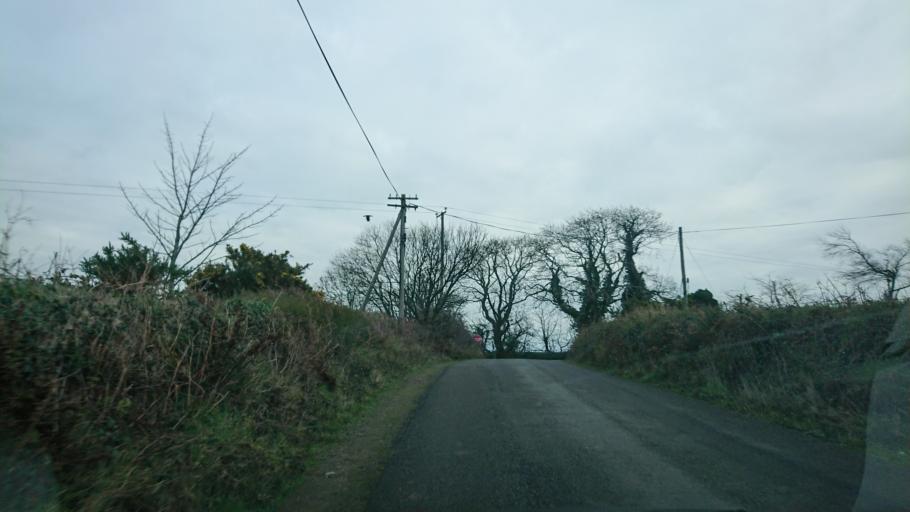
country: IE
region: Leinster
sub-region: Kilkenny
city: Mooncoin
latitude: 52.2105
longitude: -7.2637
